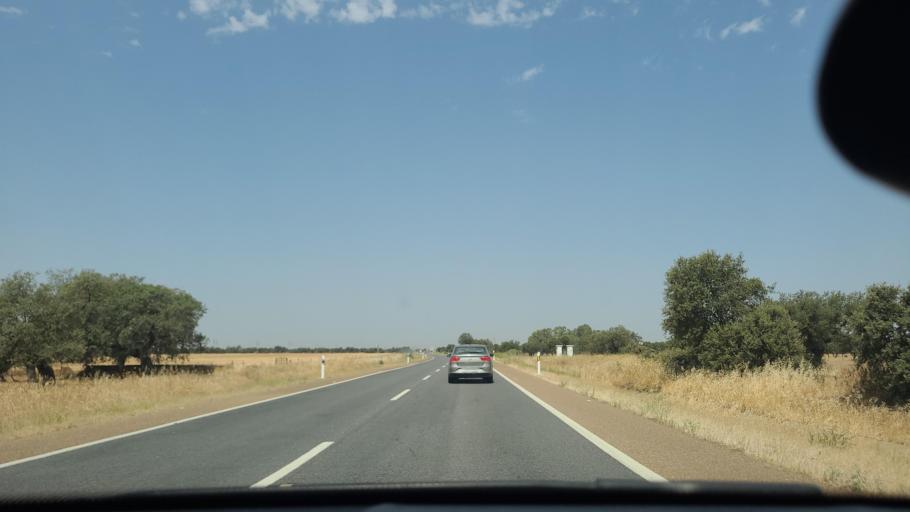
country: ES
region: Extremadura
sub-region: Provincia de Badajoz
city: Entrin Bajo
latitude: 38.6655
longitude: -6.7372
